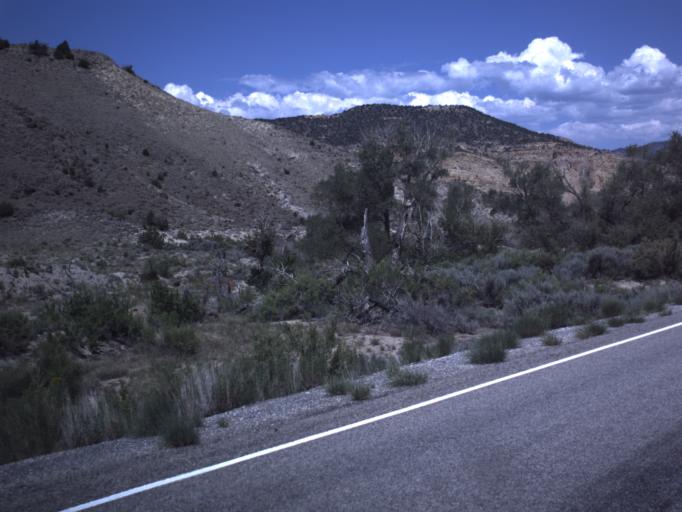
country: US
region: Utah
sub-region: Emery County
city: Ferron
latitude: 38.7742
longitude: -111.3484
